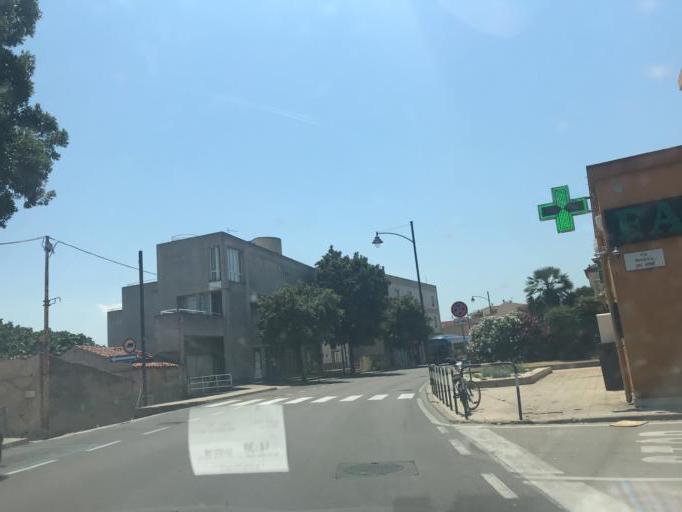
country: IT
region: Sardinia
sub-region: Provincia di Olbia-Tempio
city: Olbia
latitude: 40.9192
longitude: 9.4969
